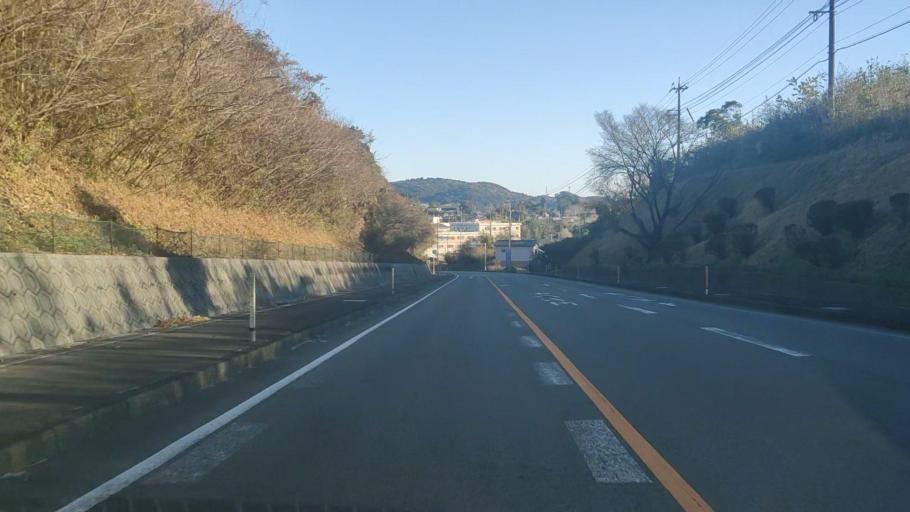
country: JP
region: Miyazaki
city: Takanabe
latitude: 32.3280
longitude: 131.6018
